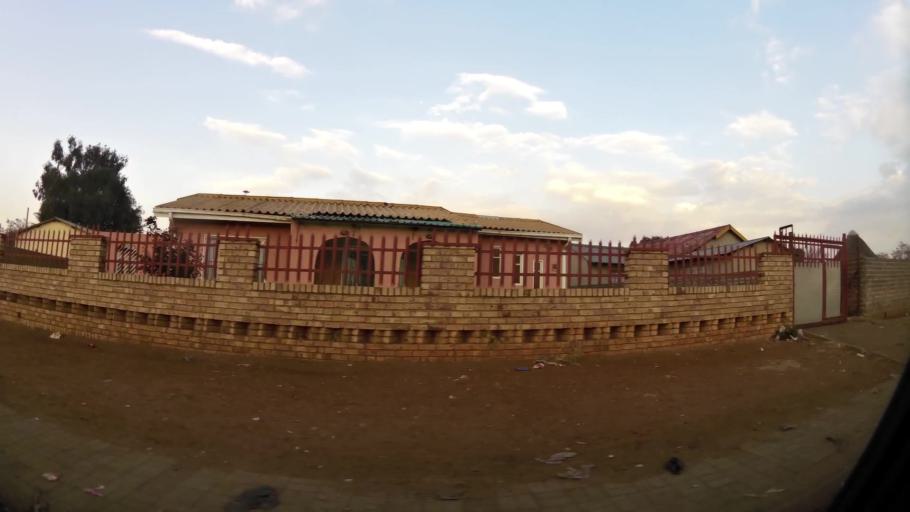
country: ZA
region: Gauteng
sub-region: City of Johannesburg Metropolitan Municipality
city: Orange Farm
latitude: -26.5524
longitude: 27.8402
